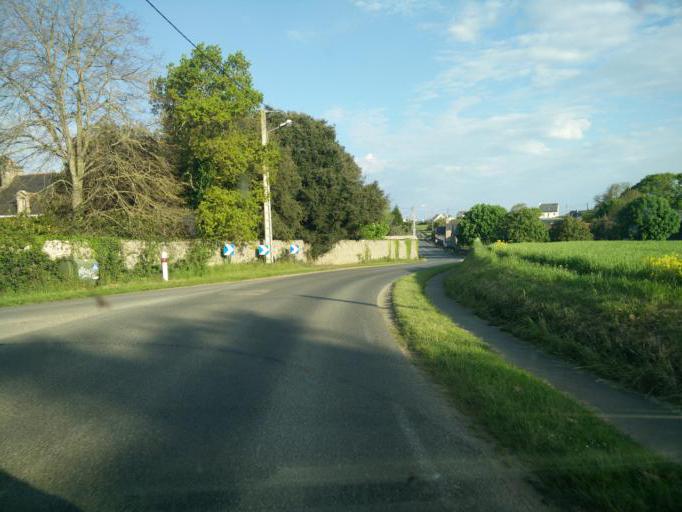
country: FR
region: Brittany
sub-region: Departement des Cotes-d'Armor
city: Erquy
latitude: 48.6244
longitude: -2.4438
